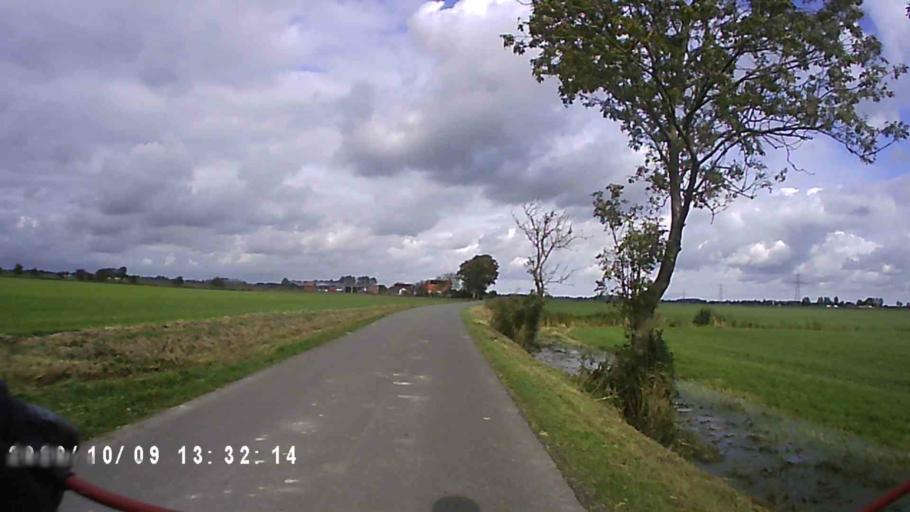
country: NL
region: Groningen
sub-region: Gemeente Zuidhorn
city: Aduard
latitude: 53.2839
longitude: 6.4731
